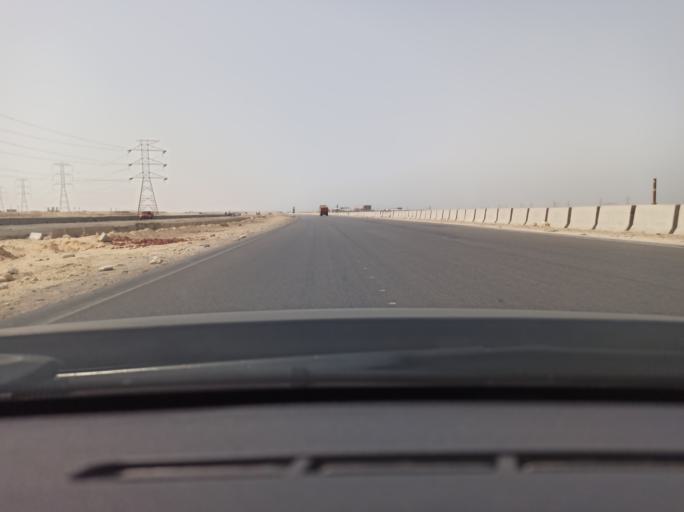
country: EG
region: Muhafazat al Fayyum
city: Al Wasitah
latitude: 29.3864
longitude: 31.3175
